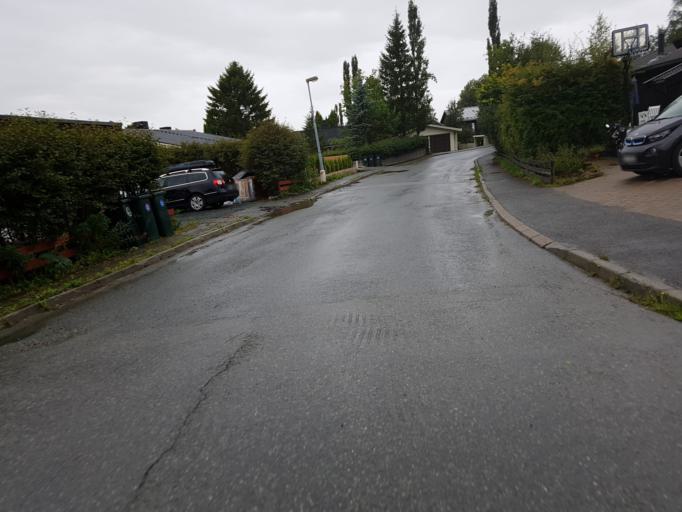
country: NO
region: Sor-Trondelag
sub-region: Trondheim
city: Trondheim
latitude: 63.4030
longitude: 10.4544
